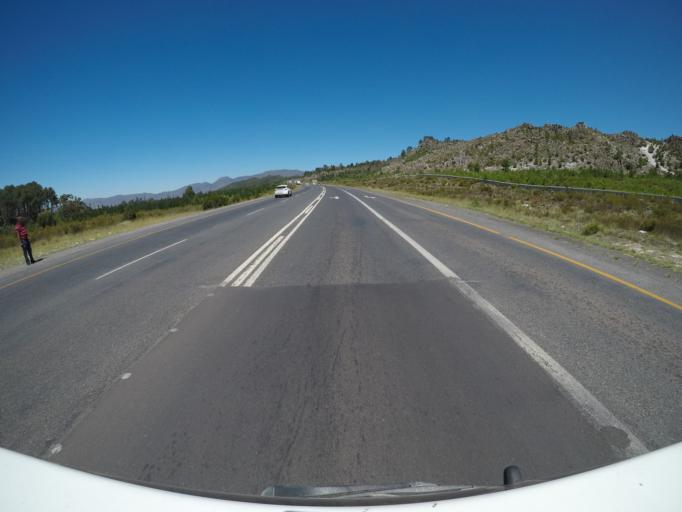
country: ZA
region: Western Cape
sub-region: Overberg District Municipality
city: Grabouw
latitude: -34.1632
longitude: 19.0080
